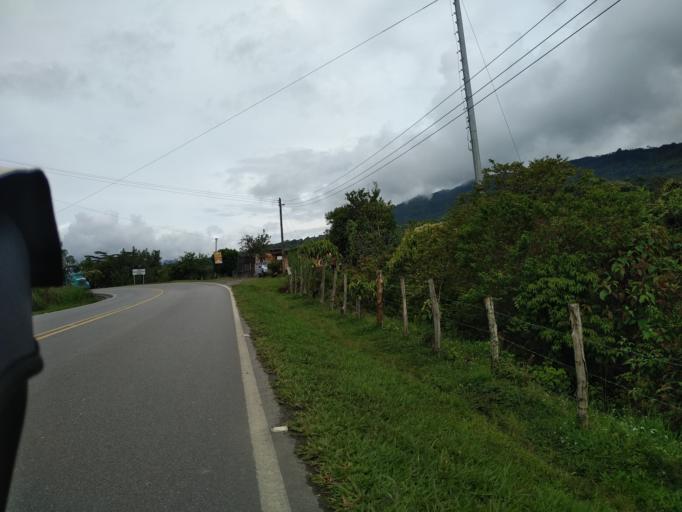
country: CO
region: Santander
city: Suaita
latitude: 6.0966
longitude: -73.3822
